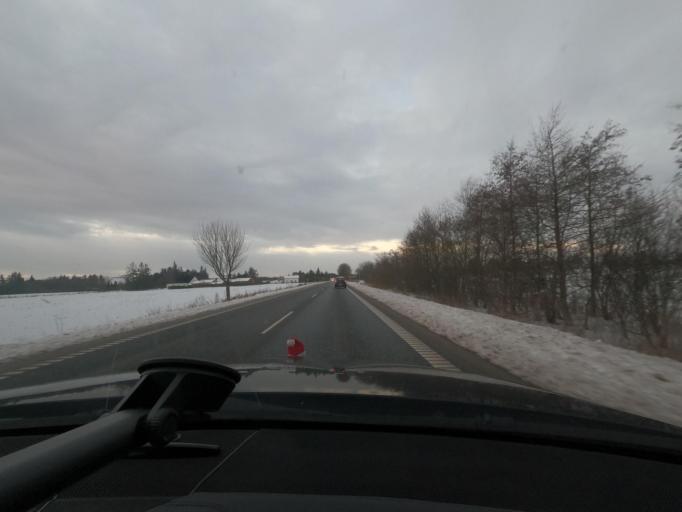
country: DK
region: South Denmark
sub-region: Aabenraa Kommune
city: Krusa
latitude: 54.8682
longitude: 9.4573
